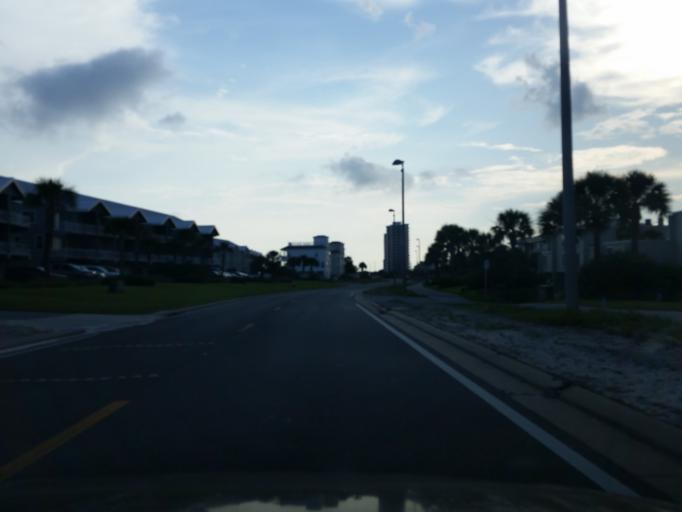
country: US
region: Florida
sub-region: Santa Rosa County
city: Gulf Breeze
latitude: 30.3294
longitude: -87.1537
